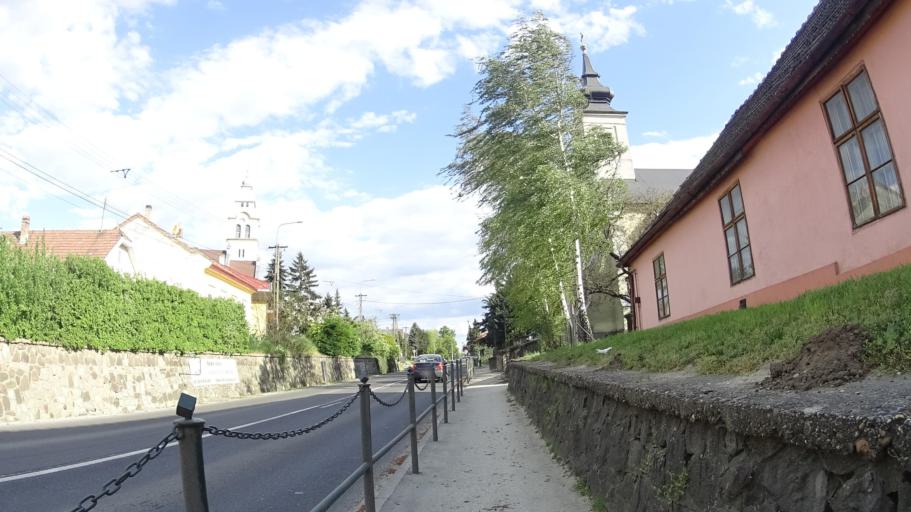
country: HU
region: Pest
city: Szada
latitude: 47.6375
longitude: 19.3108
